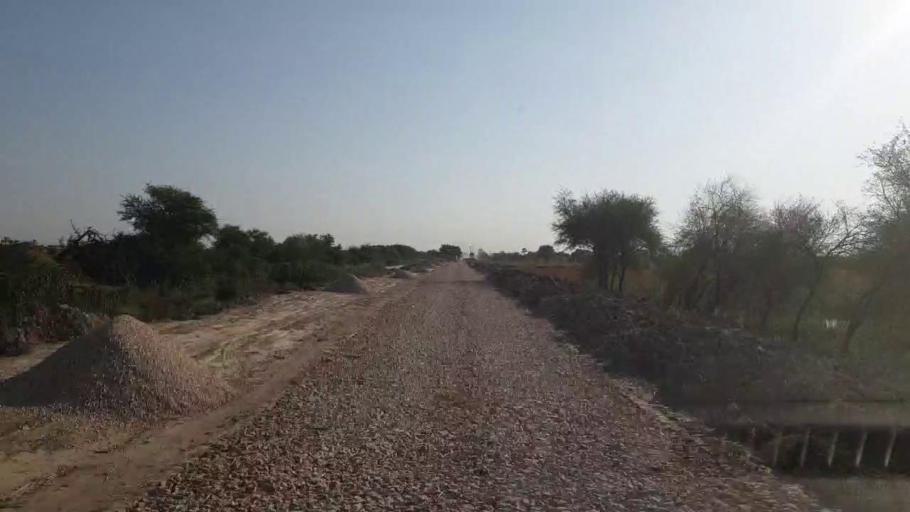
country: PK
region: Sindh
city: Talhar
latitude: 24.9285
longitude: 68.7485
